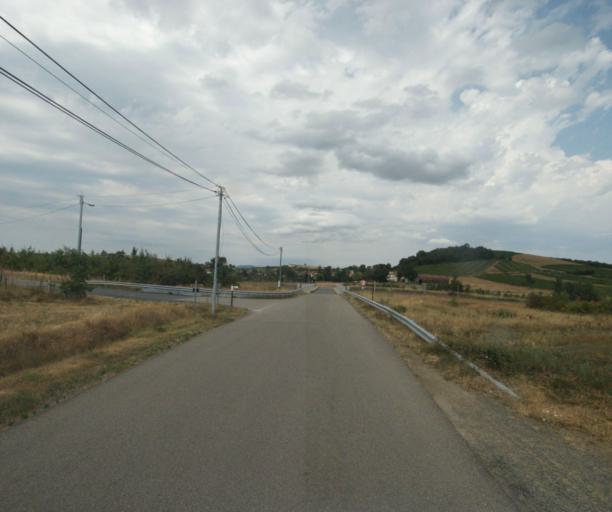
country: FR
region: Rhone-Alpes
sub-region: Departement du Rhone
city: Bully
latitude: 45.8658
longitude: 4.5772
